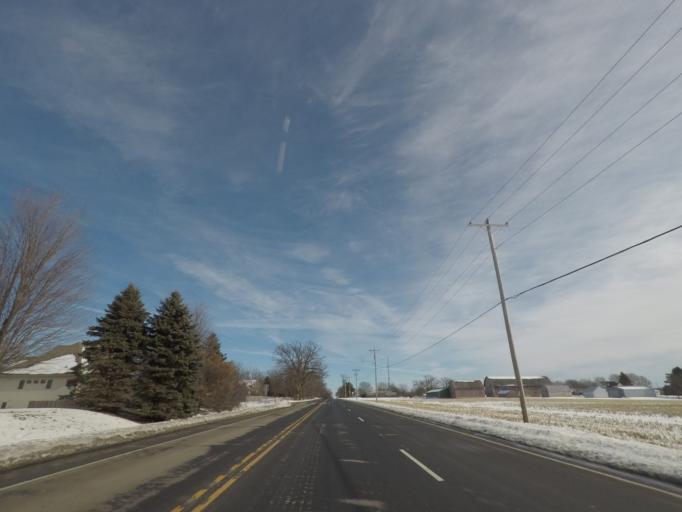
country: US
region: Wisconsin
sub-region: Dane County
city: Fitchburg
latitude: 43.0013
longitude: -89.4496
